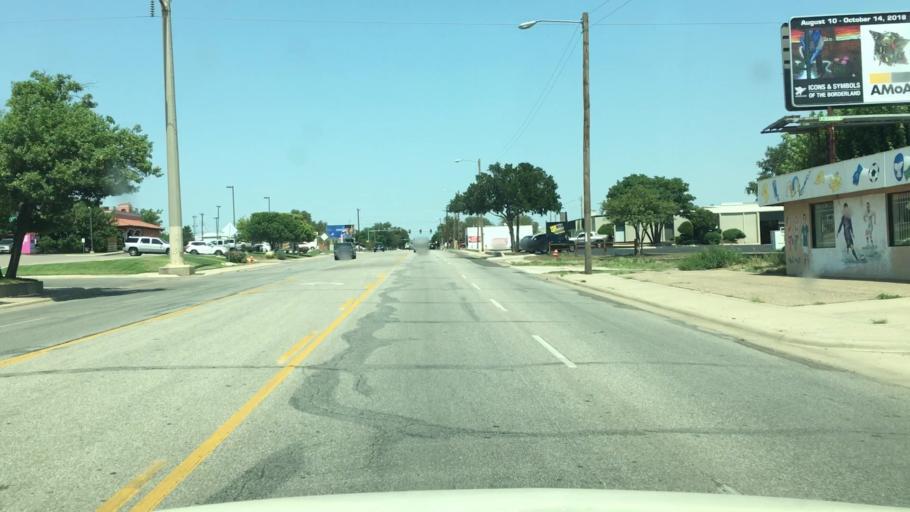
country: US
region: Texas
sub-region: Potter County
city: Amarillo
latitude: 35.1982
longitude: -101.8165
